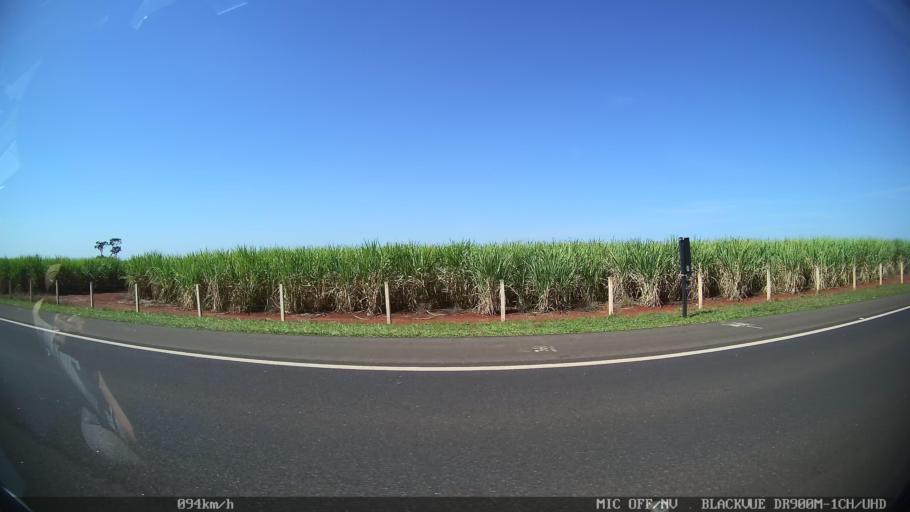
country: BR
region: Sao Paulo
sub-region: Batatais
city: Batatais
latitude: -20.7761
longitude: -47.5455
